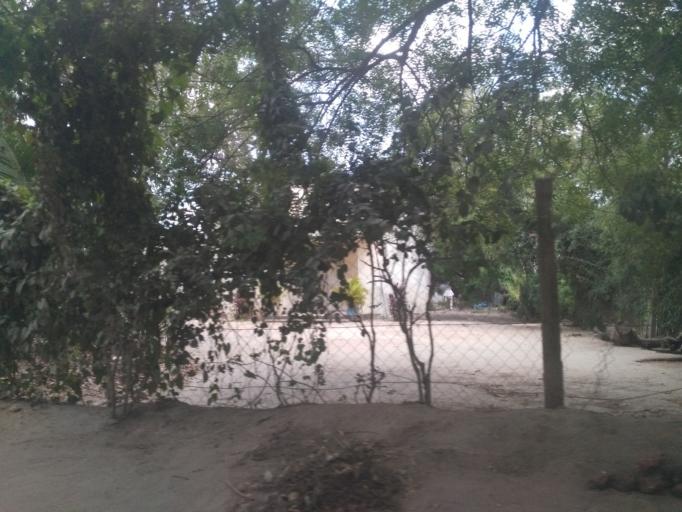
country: TZ
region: Dar es Salaam
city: Dar es Salaam
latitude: -6.8470
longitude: 39.2701
